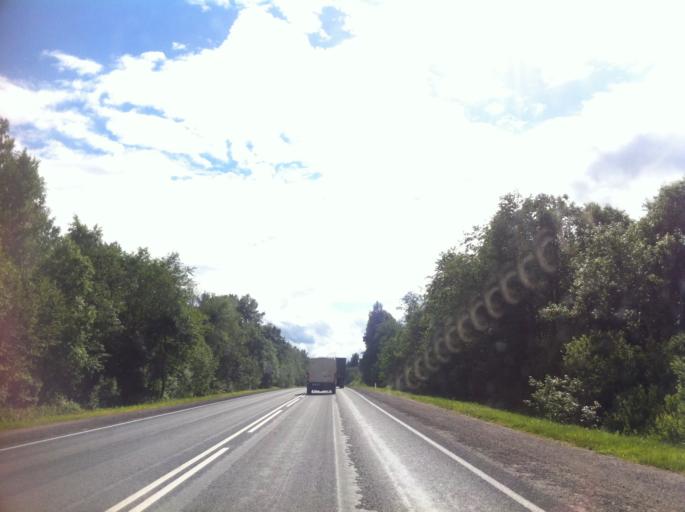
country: RU
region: Pskov
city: Strugi-Krasnyye
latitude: 58.0841
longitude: 29.0392
